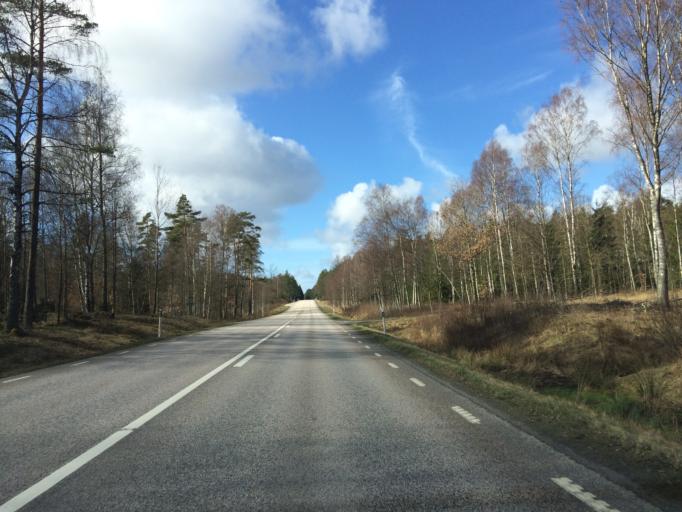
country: SE
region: Halland
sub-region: Laholms Kommun
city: Knared
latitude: 56.4883
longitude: 13.4178
